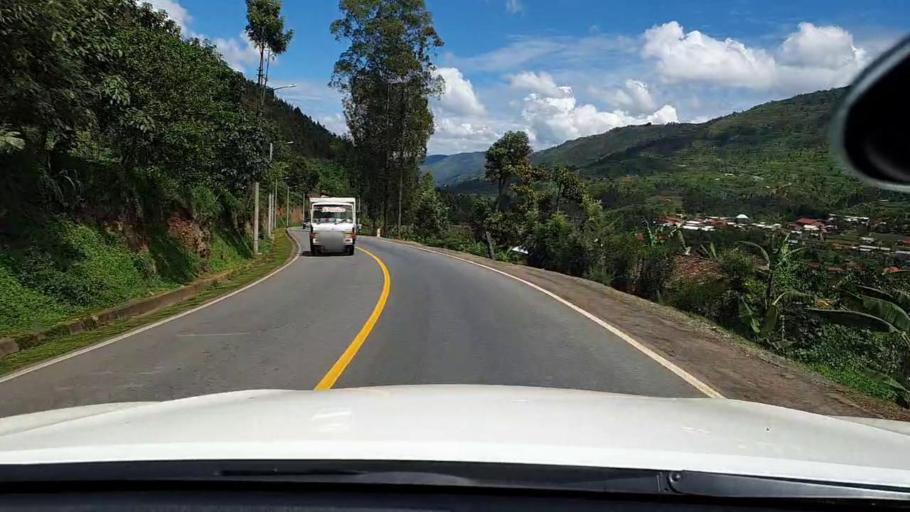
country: RW
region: Kigali
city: Kigali
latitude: -1.7703
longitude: 29.9289
